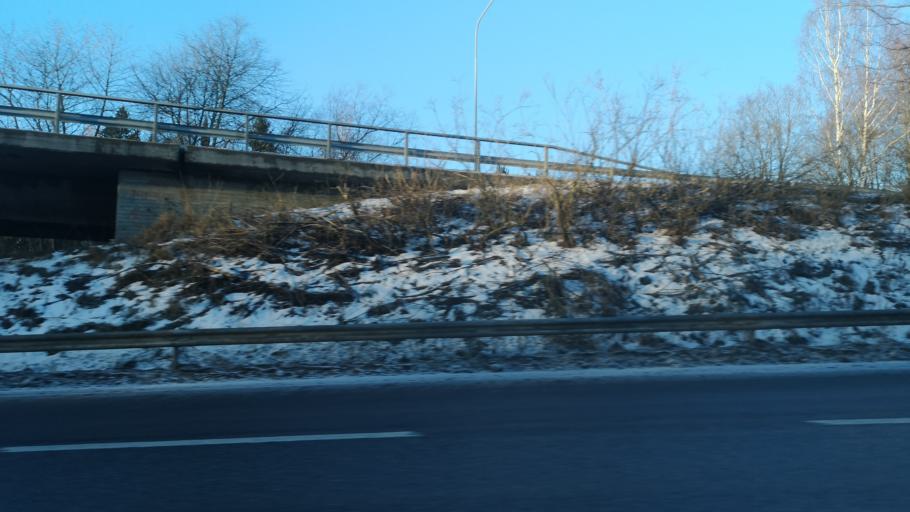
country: FI
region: Southern Savonia
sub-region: Mikkeli
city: Mikkeli
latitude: 61.6402
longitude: 27.0745
